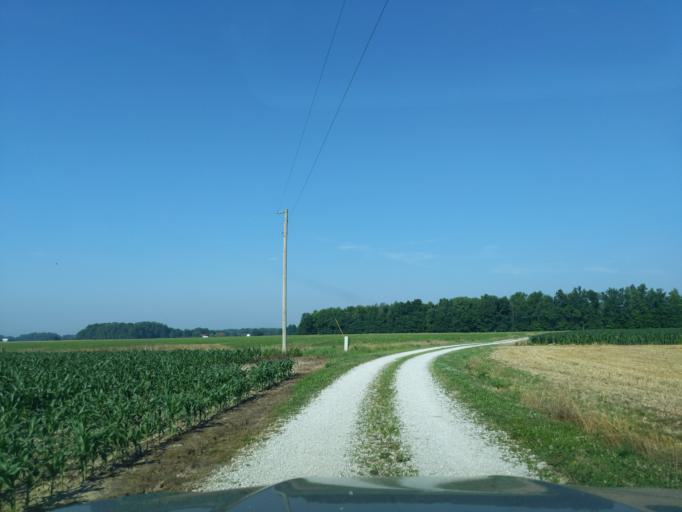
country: US
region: Indiana
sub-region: Decatur County
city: Greensburg
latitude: 39.2164
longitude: -85.4157
